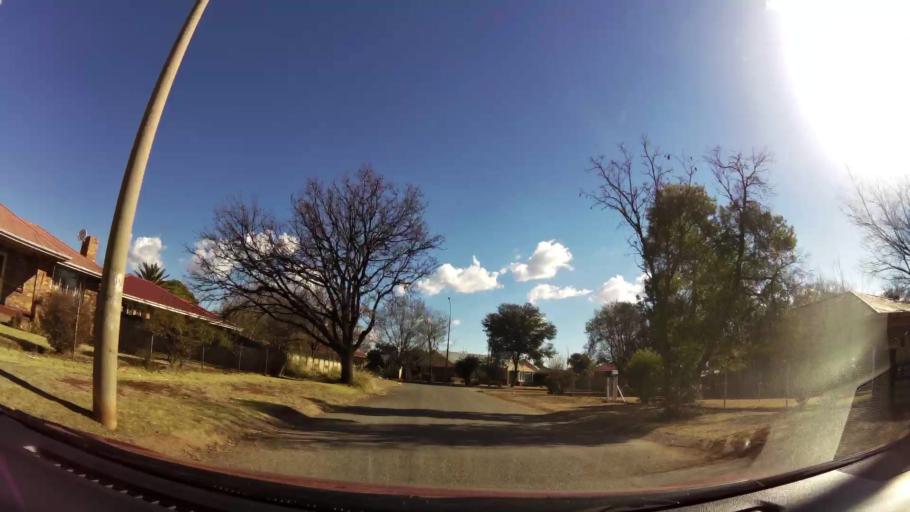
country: ZA
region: Gauteng
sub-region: West Rand District Municipality
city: Carletonville
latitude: -26.3621
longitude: 27.3624
